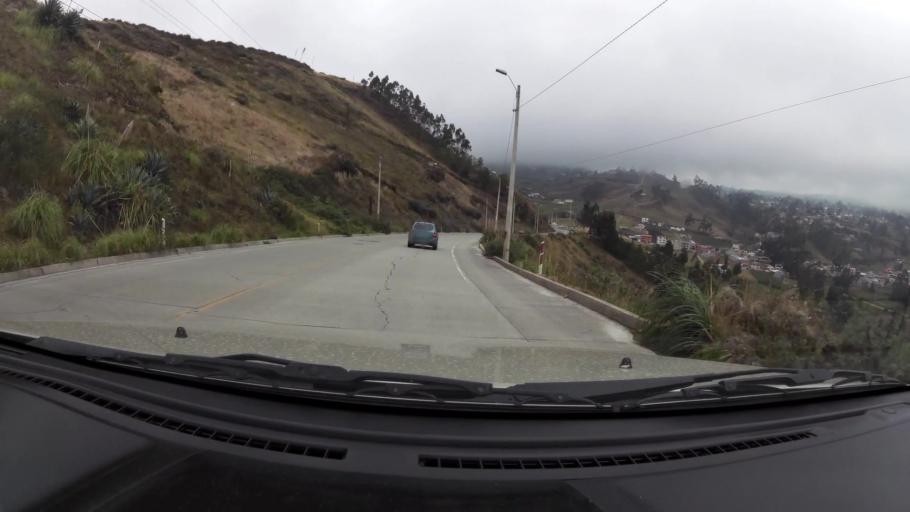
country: EC
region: Canar
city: Canar
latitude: -2.5656
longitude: -78.9310
